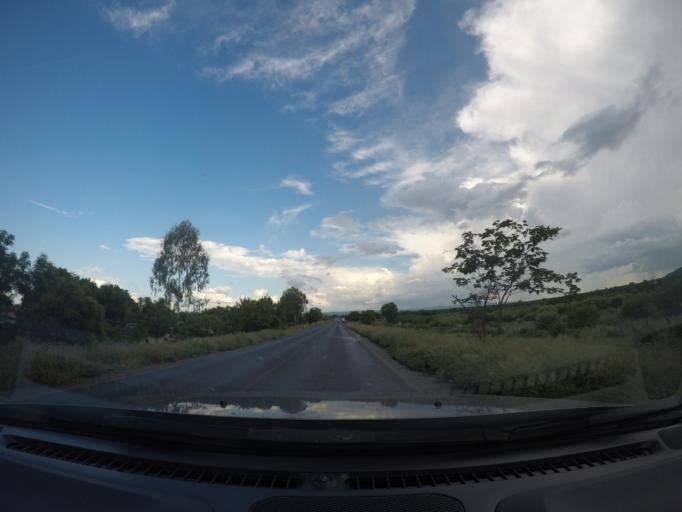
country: BR
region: Bahia
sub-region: Ibotirama
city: Ibotirama
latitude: -12.1349
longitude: -43.3322
